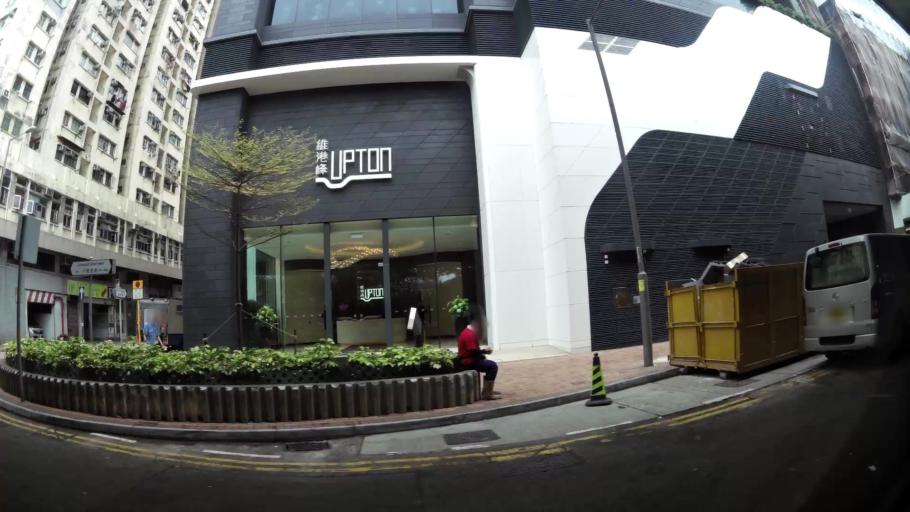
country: HK
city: Hong Kong
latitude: 22.2877
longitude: 114.1371
